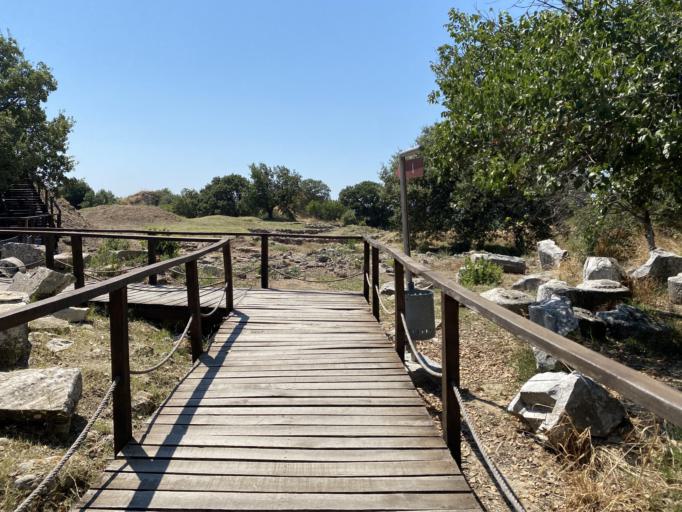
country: TR
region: Canakkale
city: Intepe
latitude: 39.9578
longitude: 26.2389
